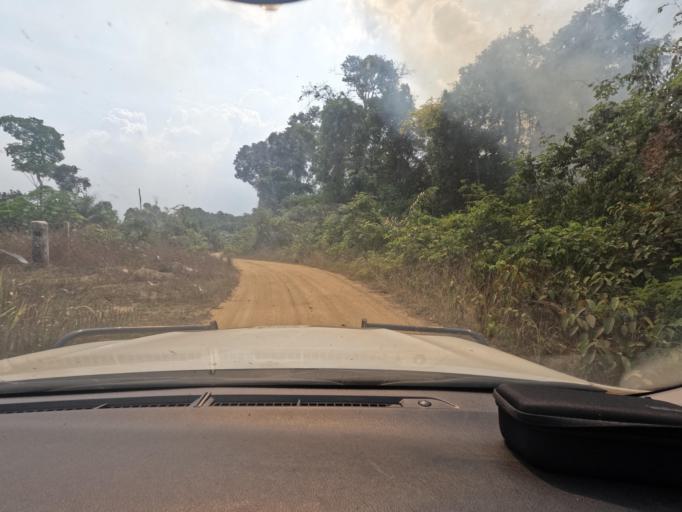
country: BR
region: Rondonia
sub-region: Porto Velho
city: Porto Velho
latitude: -8.7727
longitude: -63.2273
